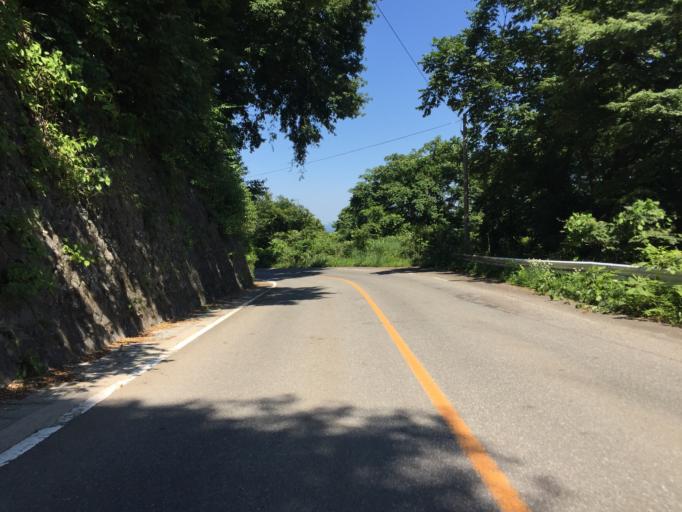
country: JP
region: Fukushima
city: Fukushima-shi
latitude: 37.7534
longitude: 140.3497
